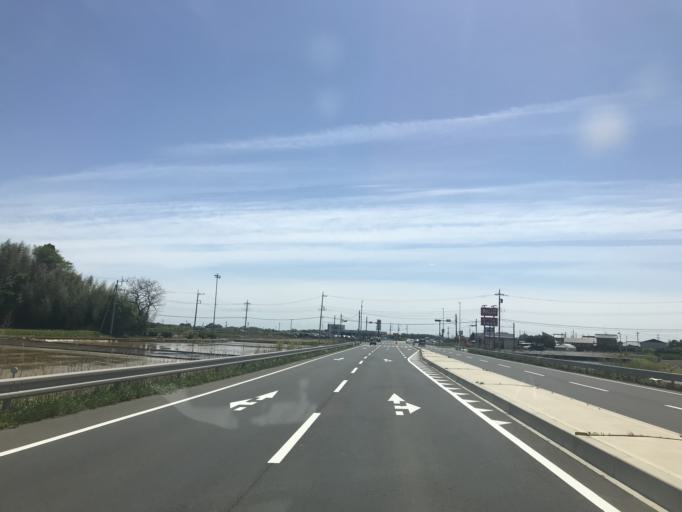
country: JP
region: Ibaraki
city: Ishige
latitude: 36.1649
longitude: 139.9945
